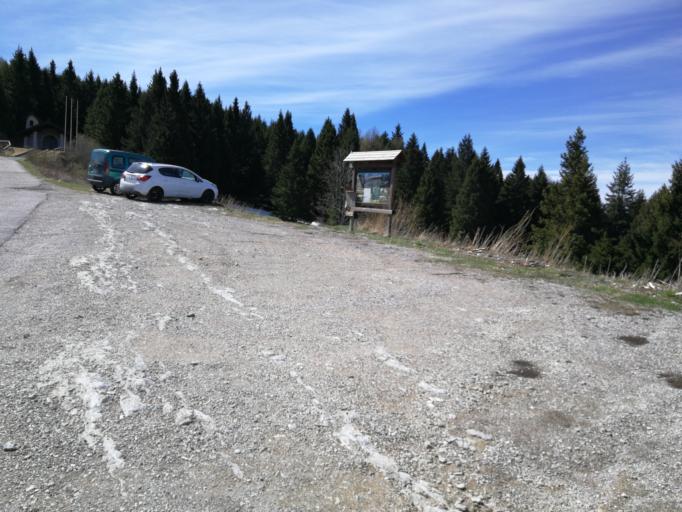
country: IT
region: Trentino-Alto Adige
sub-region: Provincia di Trento
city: Marco
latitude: 45.8074
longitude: 11.0585
